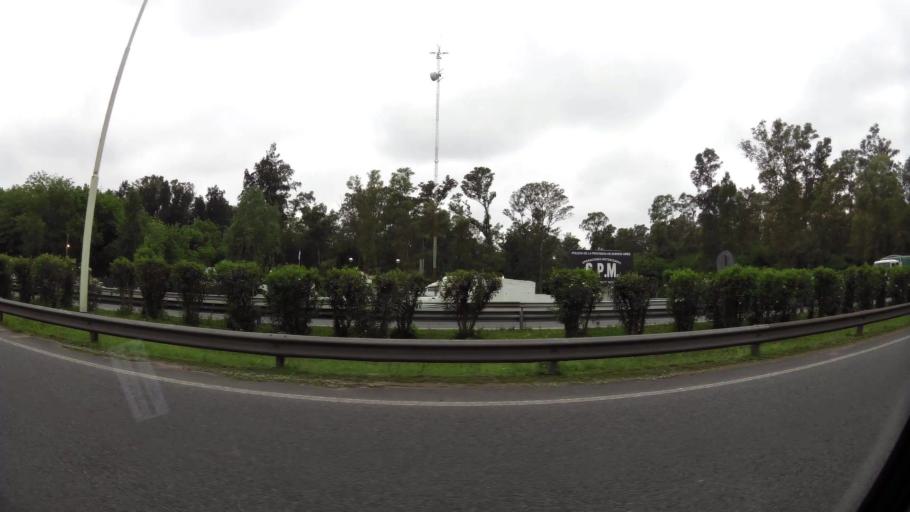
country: AR
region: Buenos Aires
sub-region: Partido de Ezeiza
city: Ezeiza
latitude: -34.7900
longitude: -58.5183
